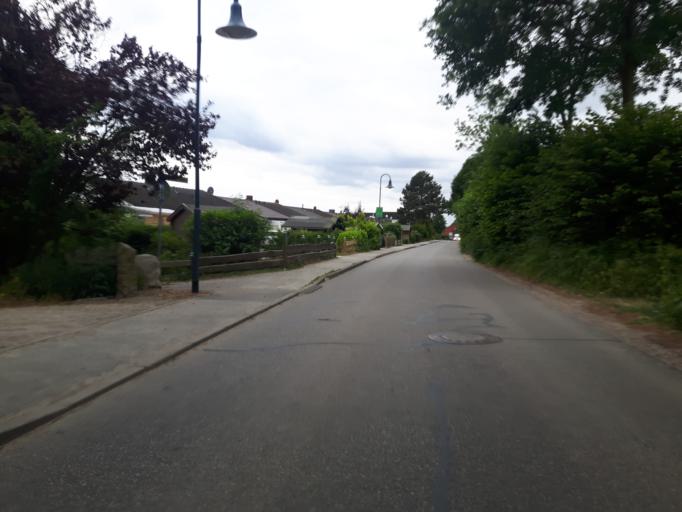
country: DE
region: Schleswig-Holstein
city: Schashagen
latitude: 54.1006
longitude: 10.8915
